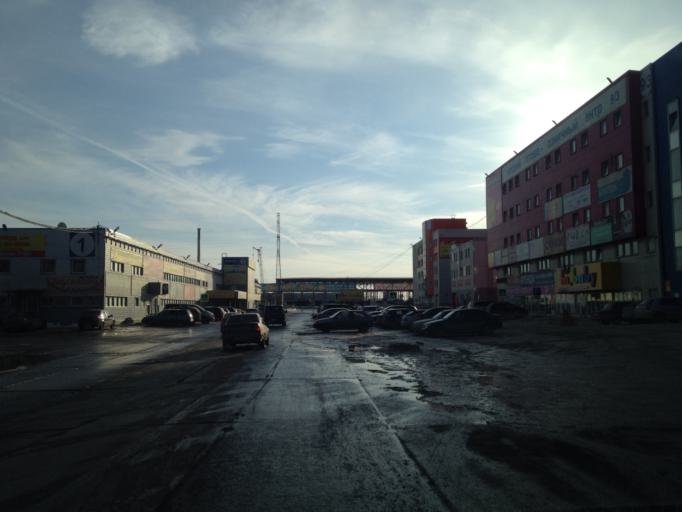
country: RU
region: Sverdlovsk
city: Istok
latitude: 56.7576
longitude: 60.7575
